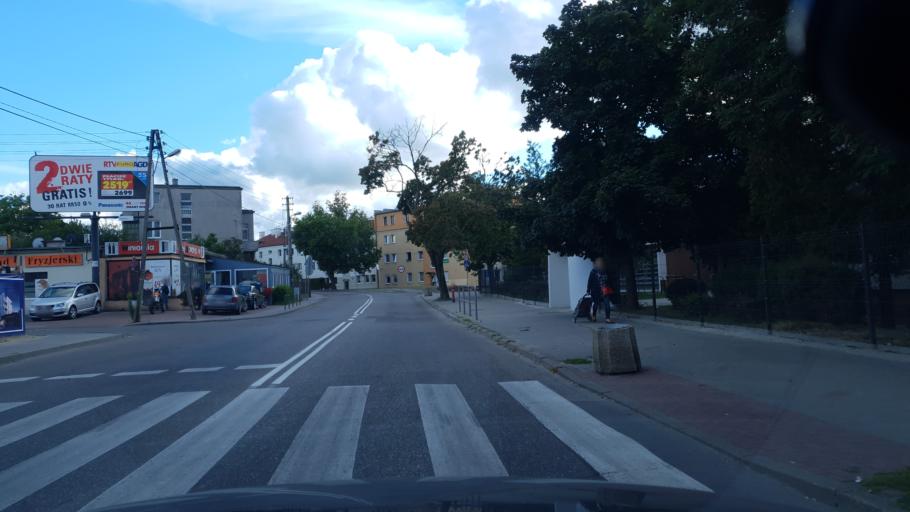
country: PL
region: Pomeranian Voivodeship
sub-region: Gdynia
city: Gdynia
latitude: 54.5030
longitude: 18.5417
